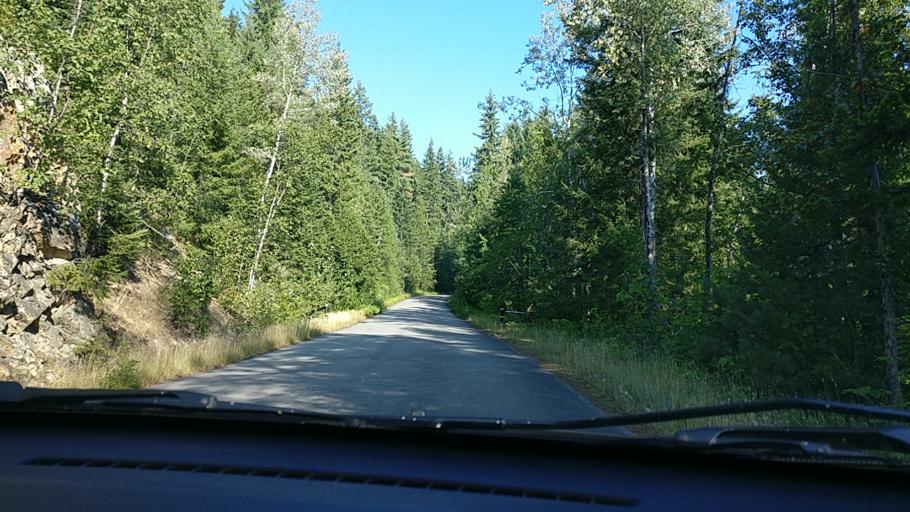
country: CA
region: British Columbia
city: Revelstoke
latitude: 51.0080
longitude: -118.1869
